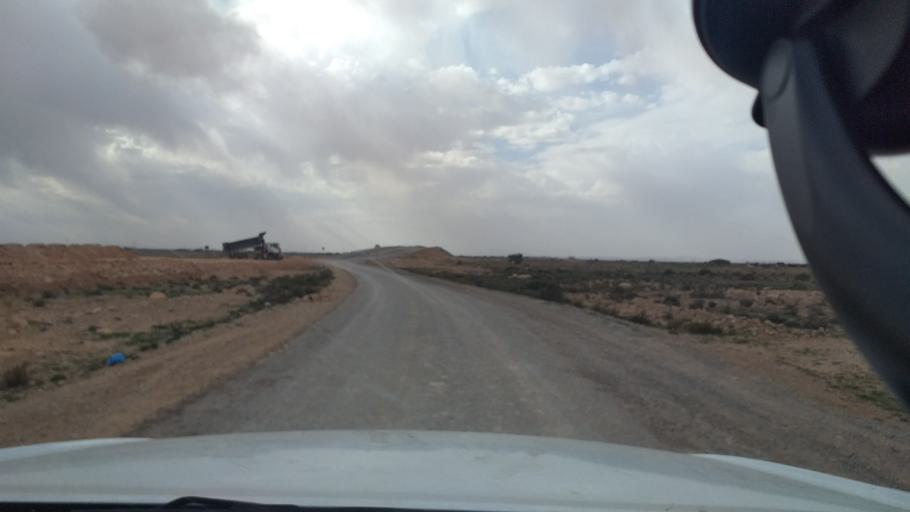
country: TN
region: Madanin
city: Medenine
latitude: 33.3040
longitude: 10.6113
